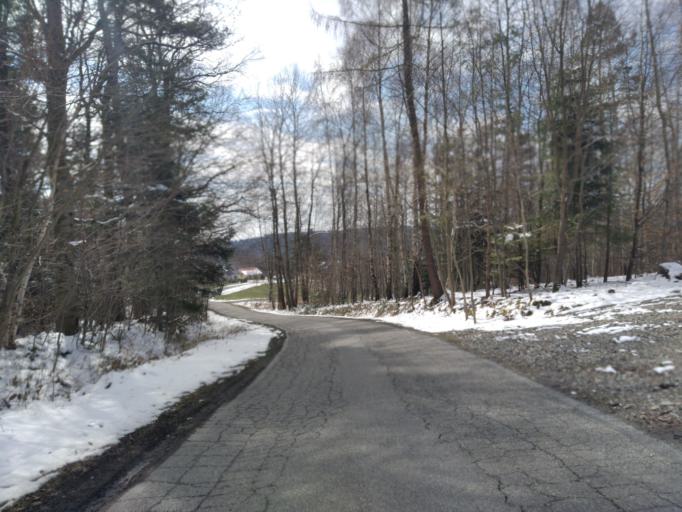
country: PL
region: Subcarpathian Voivodeship
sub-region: Powiat ropczycko-sedziszowski
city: Ropczyce
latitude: 50.0111
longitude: 21.5960
